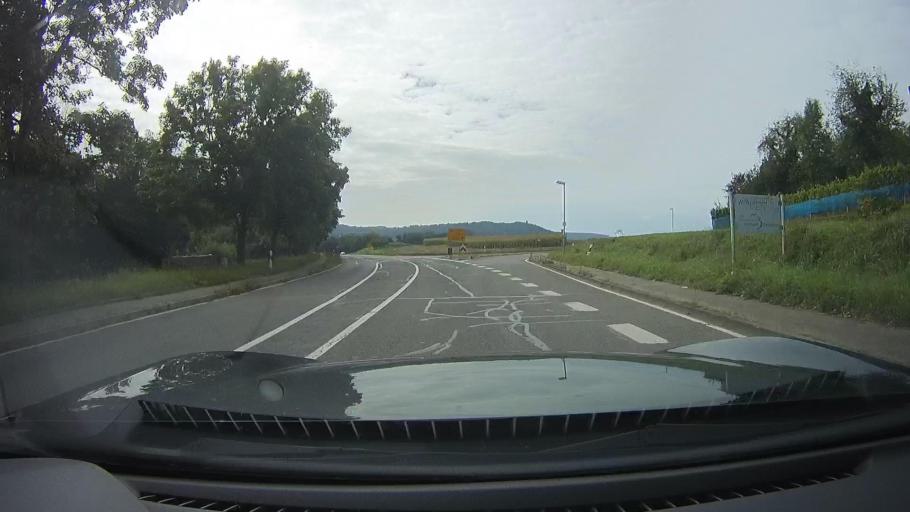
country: DE
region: Baden-Wuerttemberg
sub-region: Regierungsbezirk Stuttgart
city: Oberstenfeld
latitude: 49.0399
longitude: 9.3316
